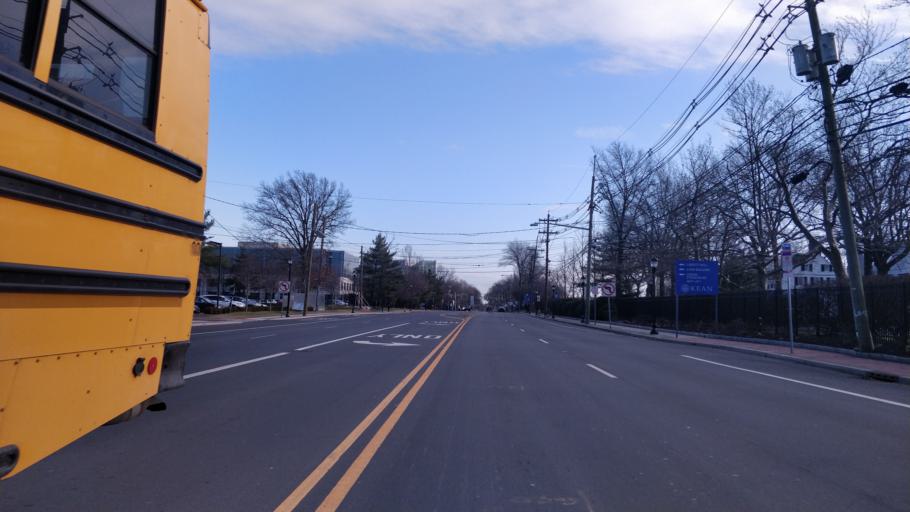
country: US
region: New Jersey
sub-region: Union County
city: Hillside
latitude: 40.6825
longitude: -74.2353
